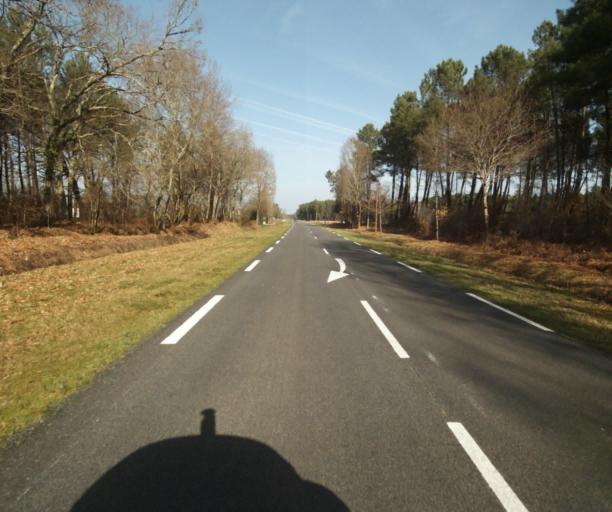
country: FR
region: Aquitaine
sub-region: Departement de la Gironde
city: Grignols
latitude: 44.1977
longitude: -0.1389
